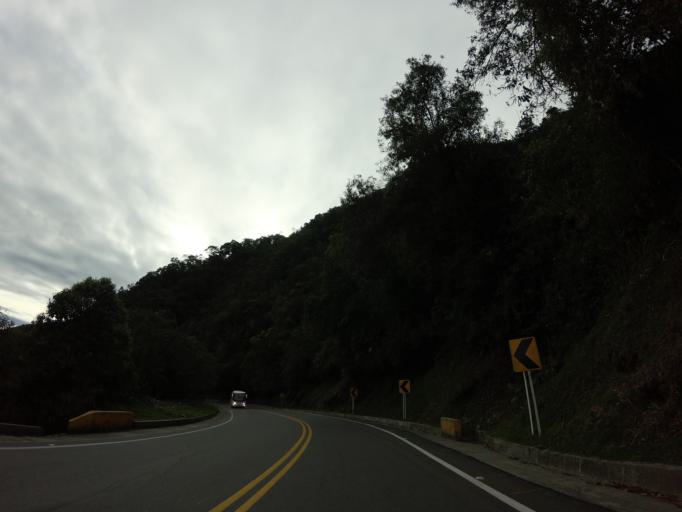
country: CO
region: Tolima
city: Herveo
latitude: 5.1119
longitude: -75.2157
